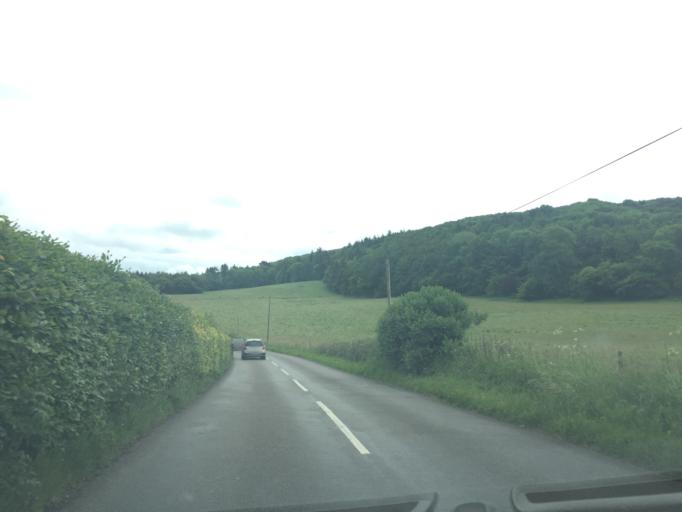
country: GB
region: England
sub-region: Dorset
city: Swanage
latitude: 50.6402
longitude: -2.0170
